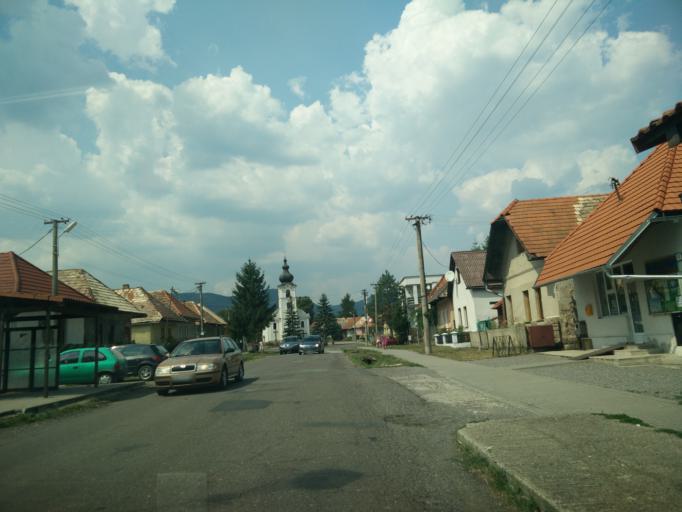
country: SK
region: Banskobystricky
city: Zarnovica
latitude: 48.5438
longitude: 18.7652
